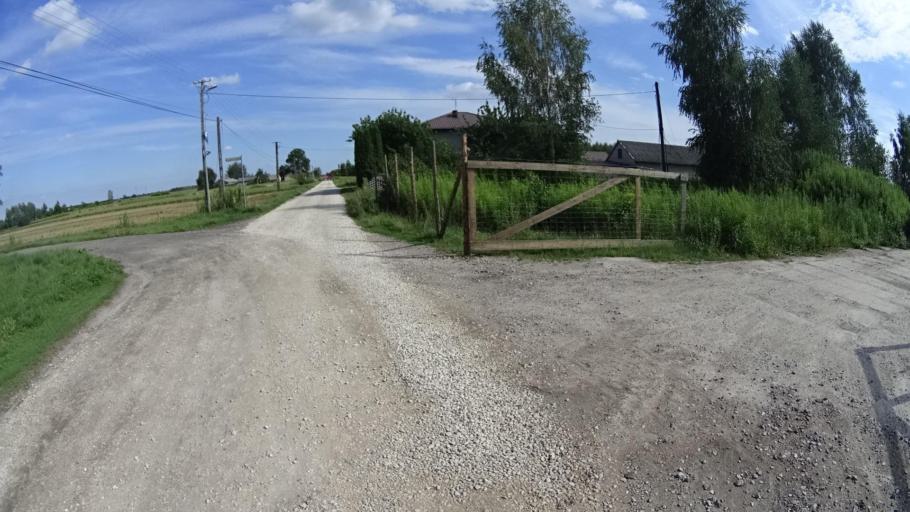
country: PL
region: Masovian Voivodeship
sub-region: Powiat piaseczynski
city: Lesznowola
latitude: 52.0661
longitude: 20.9387
